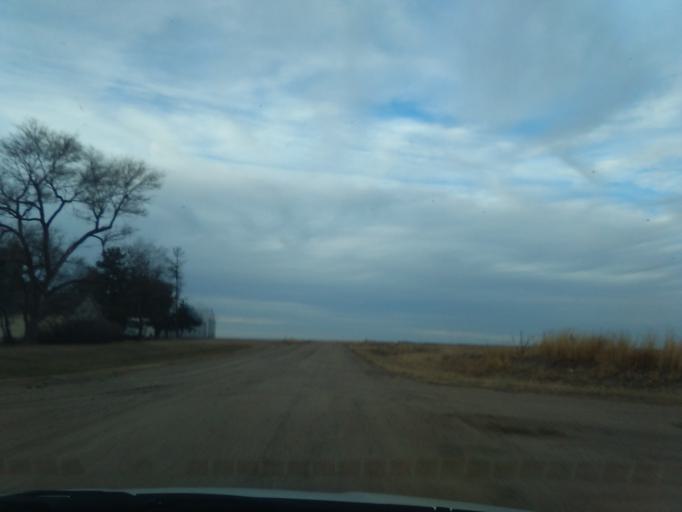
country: US
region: Nebraska
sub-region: Furnas County
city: Cambridge
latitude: 40.3219
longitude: -100.0435
